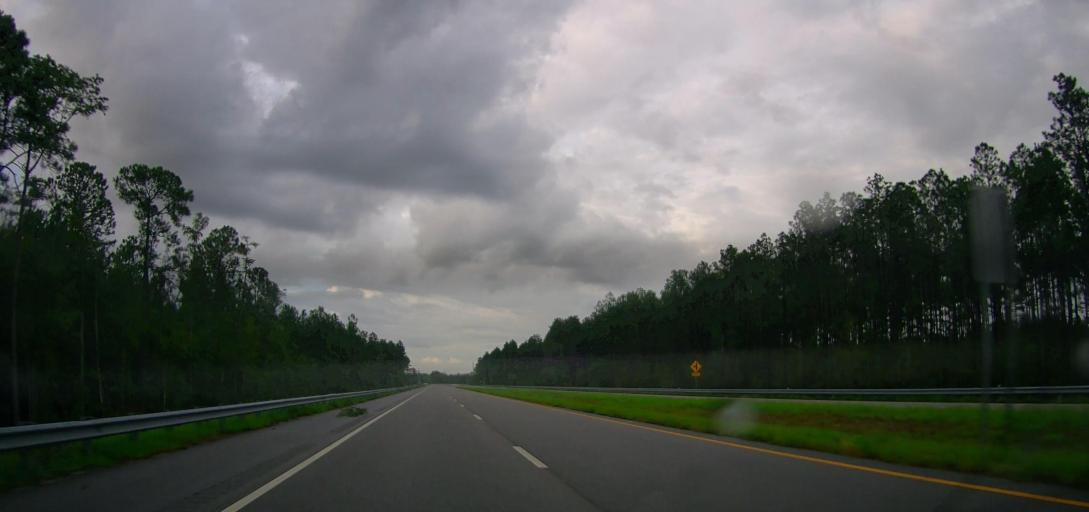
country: US
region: Georgia
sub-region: Ware County
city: Deenwood
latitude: 31.1700
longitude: -82.4108
